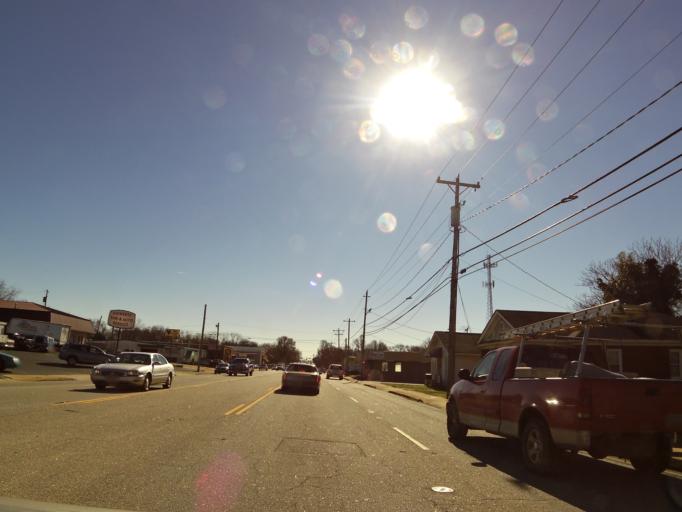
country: US
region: South Carolina
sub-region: Greenville County
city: Greenville
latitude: 34.8702
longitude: -82.4045
